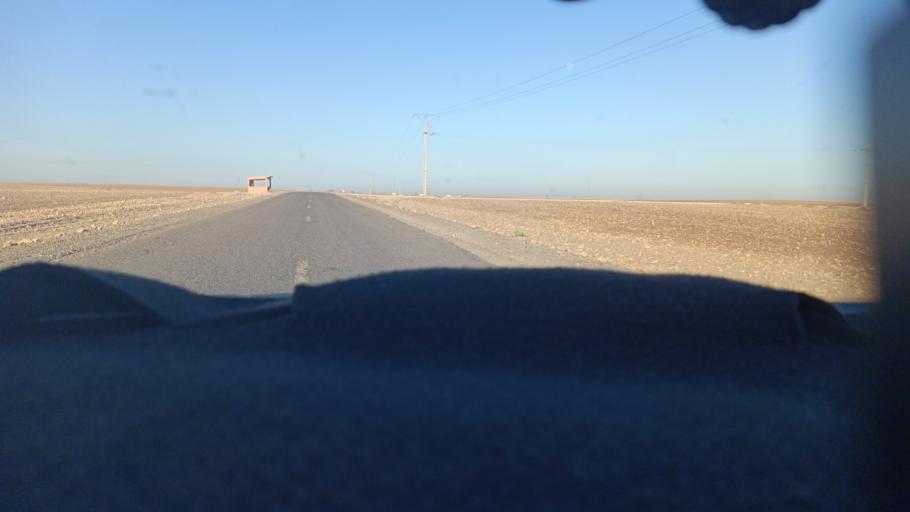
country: MA
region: Doukkala-Abda
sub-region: Safi
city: Youssoufia
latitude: 32.3712
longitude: -8.6481
